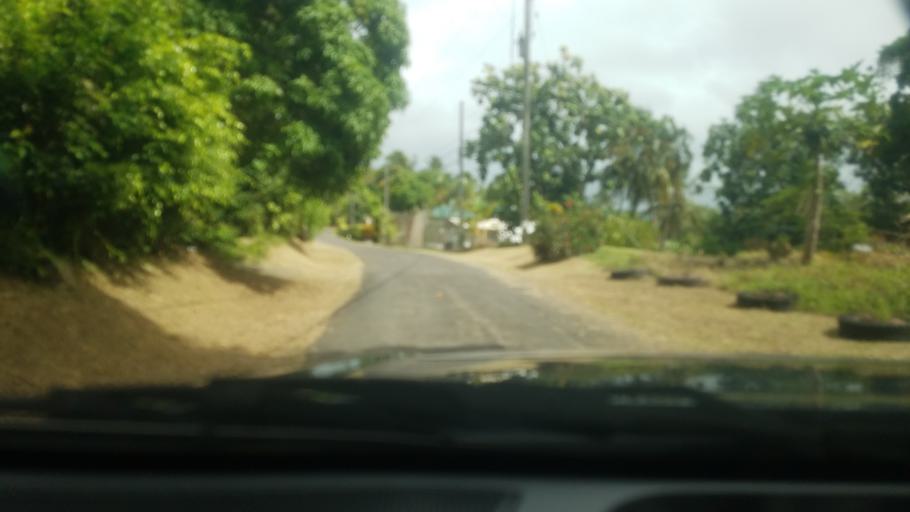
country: LC
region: Micoud Quarter
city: Micoud
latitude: 13.7950
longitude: -60.9273
